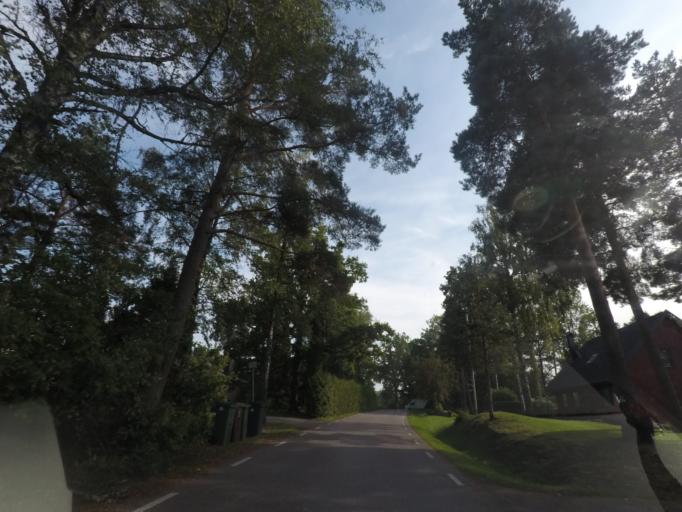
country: SE
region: Vaestmanland
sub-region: Kungsors Kommun
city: Kungsoer
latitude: 59.4893
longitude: 16.1660
